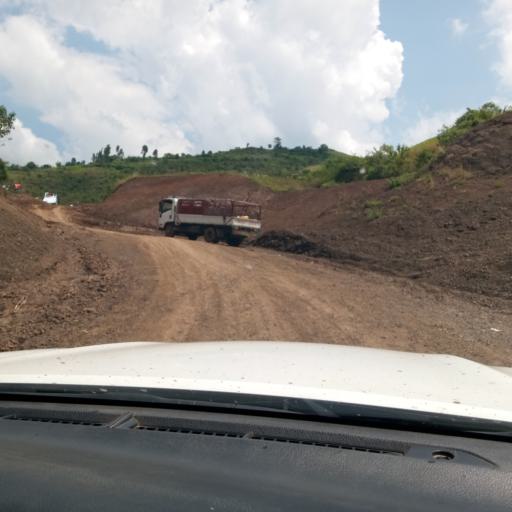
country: ET
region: Southern Nations, Nationalities, and People's Region
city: Arba Minch'
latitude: 6.3306
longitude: 37.3400
